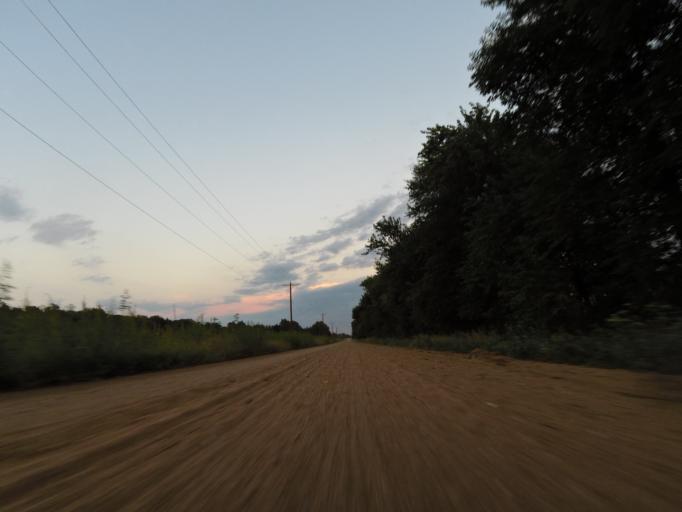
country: US
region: Kansas
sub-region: Reno County
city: South Hutchinson
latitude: 37.9555
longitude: -98.0470
